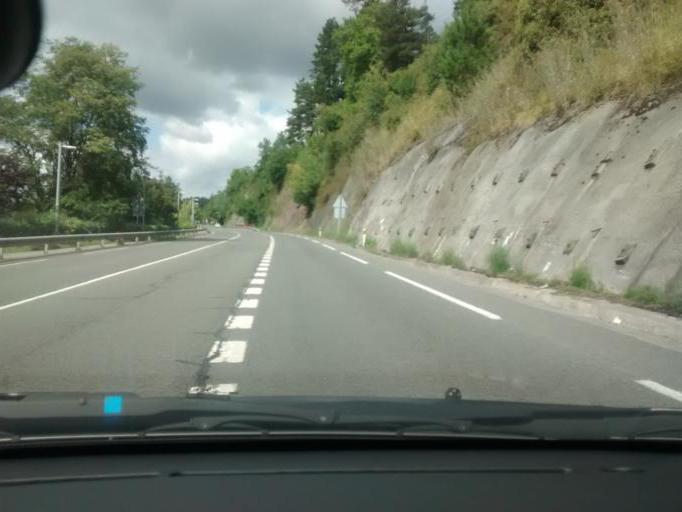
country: ES
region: Basque Country
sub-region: Provincia de Guipuzcoa
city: Eibar
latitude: 43.1908
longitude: -2.4549
